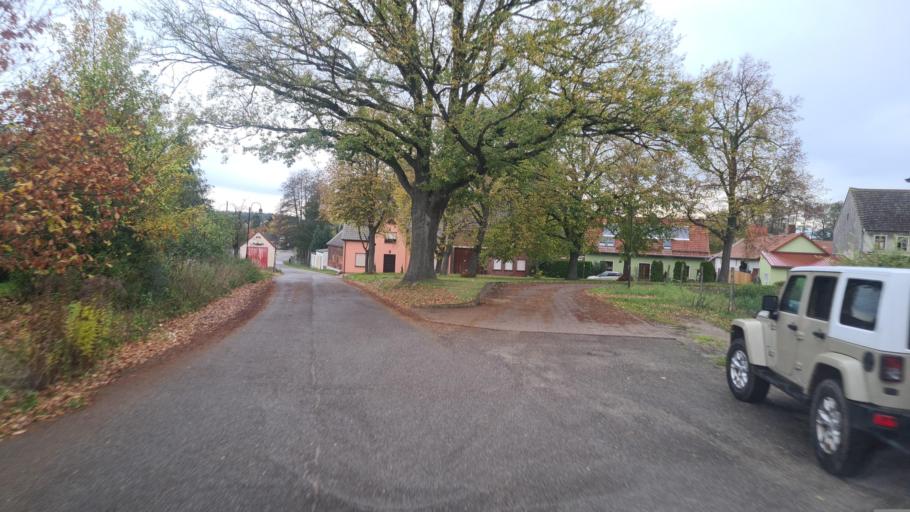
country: DE
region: Saxony-Anhalt
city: Abtsdorf
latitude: 51.9164
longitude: 12.6784
